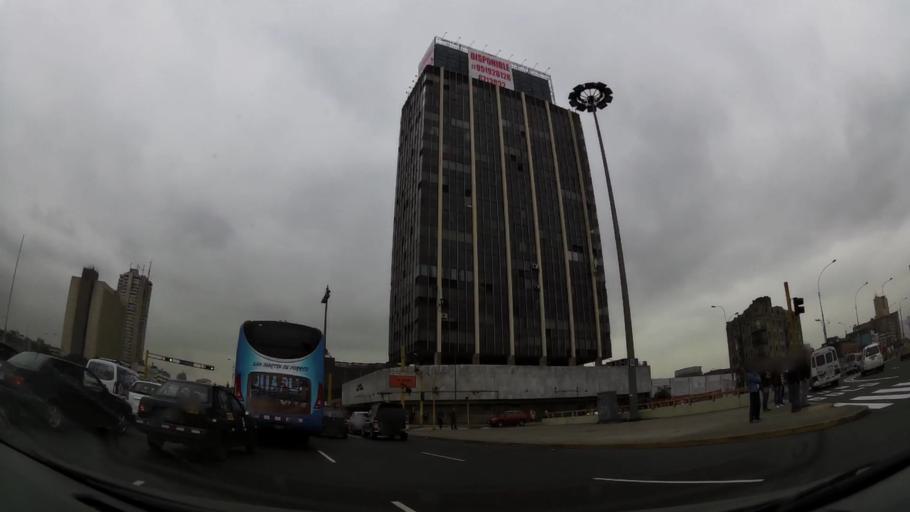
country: PE
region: Lima
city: Lima
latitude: -12.0600
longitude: -77.0354
